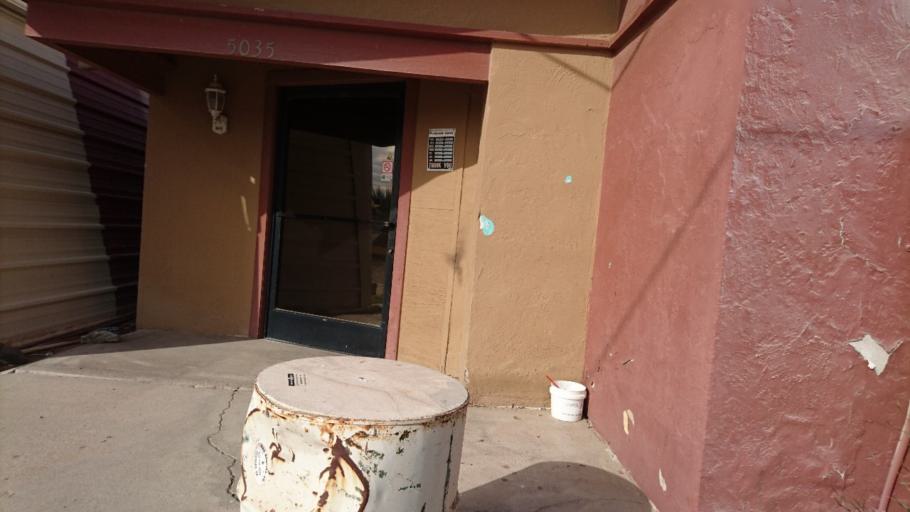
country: US
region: California
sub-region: San Bernardino County
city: Needles
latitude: 34.7790
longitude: -114.4816
